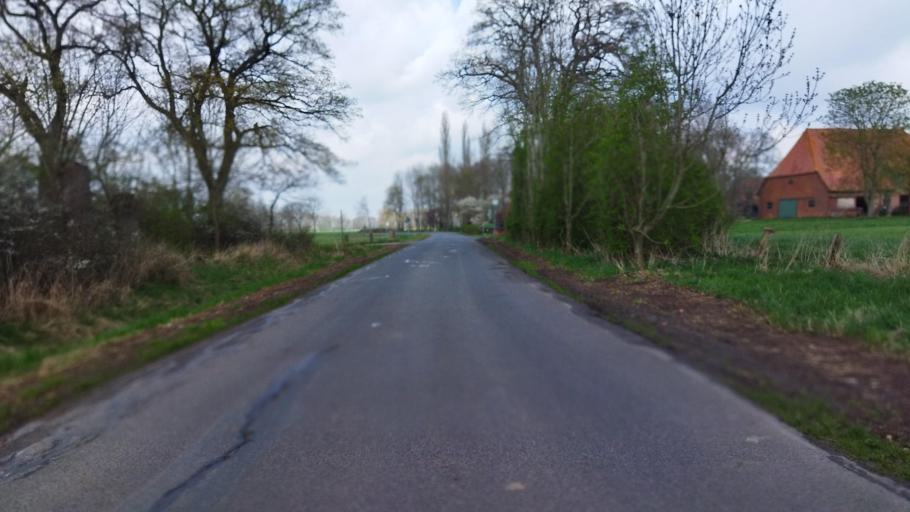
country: DE
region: Lower Saxony
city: Hilgermissen
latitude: 52.8387
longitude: 9.1894
